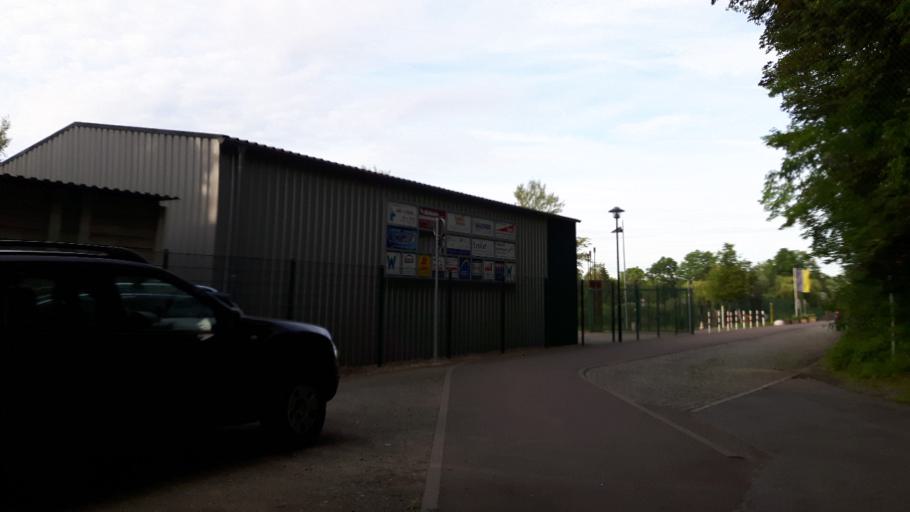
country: DE
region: Saxony-Anhalt
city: Uichteritz
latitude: 51.2049
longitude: 11.9441
